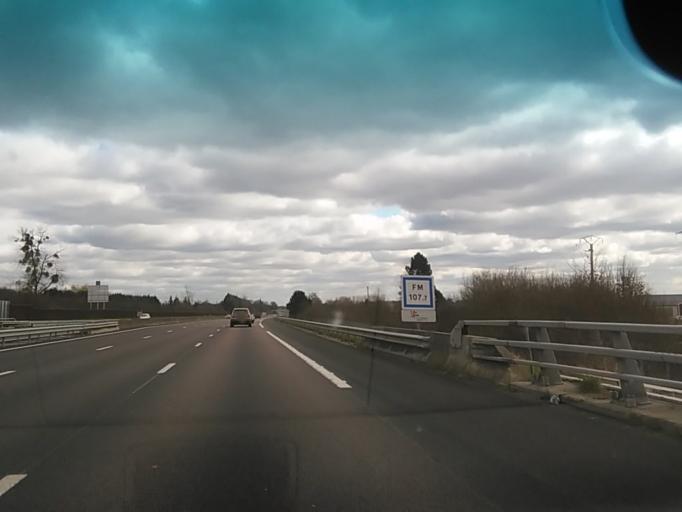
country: FR
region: Haute-Normandie
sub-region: Departement de l'Eure
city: Saint-Ouen-de-Thouberville
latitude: 49.3589
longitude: 0.8708
